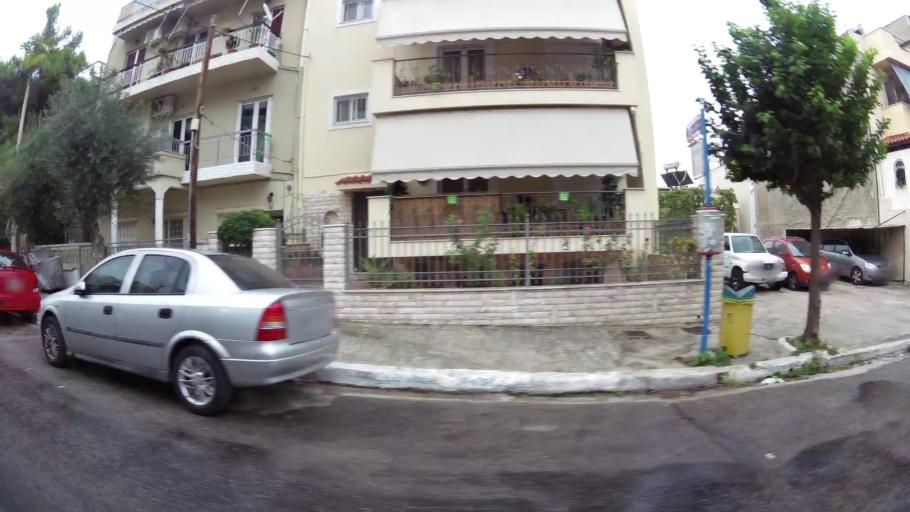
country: GR
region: Attica
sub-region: Nomos Piraios
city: Korydallos
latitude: 37.9921
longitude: 23.6506
